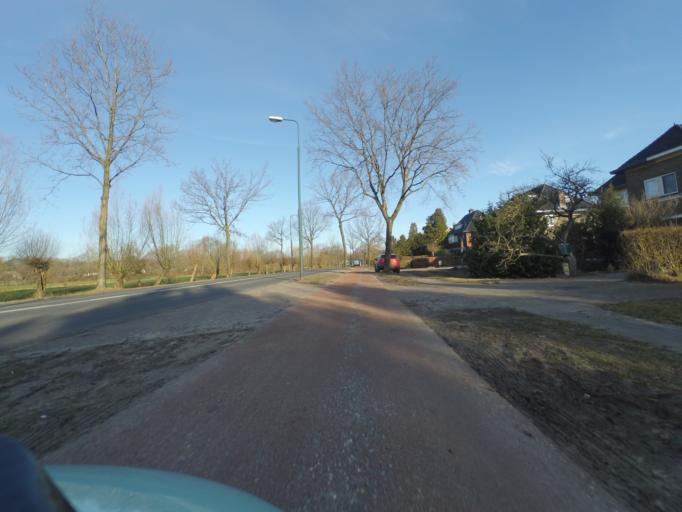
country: NL
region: Utrecht
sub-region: Gemeente Soest
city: Soest
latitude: 52.1897
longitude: 5.2959
